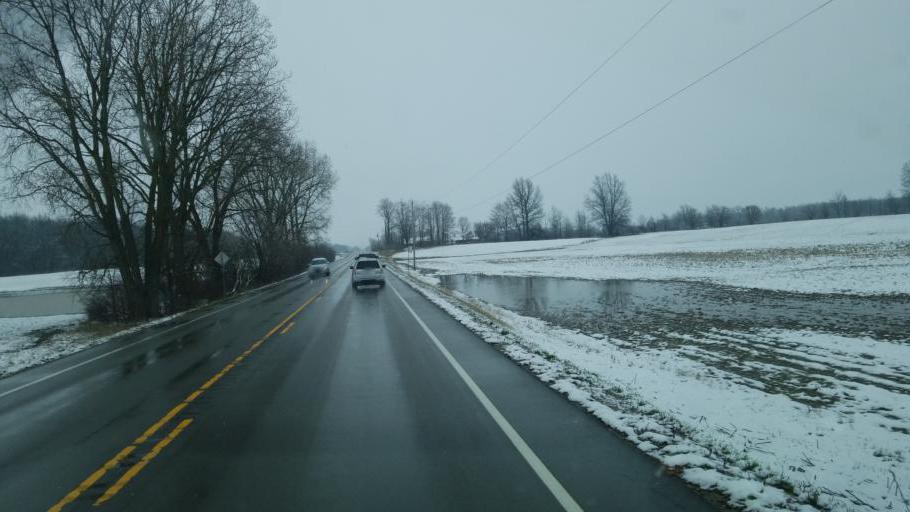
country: US
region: Indiana
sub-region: Delaware County
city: Yorktown
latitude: 40.2770
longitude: -85.4606
